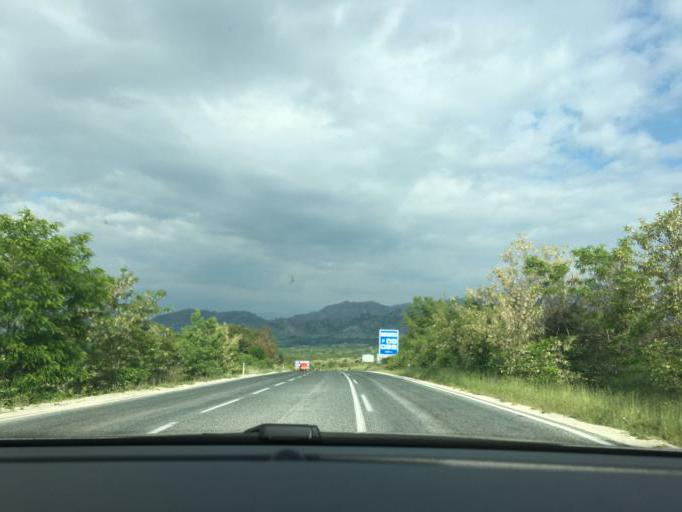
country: MK
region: Prilep
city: Prilep
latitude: 41.3699
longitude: 21.6261
